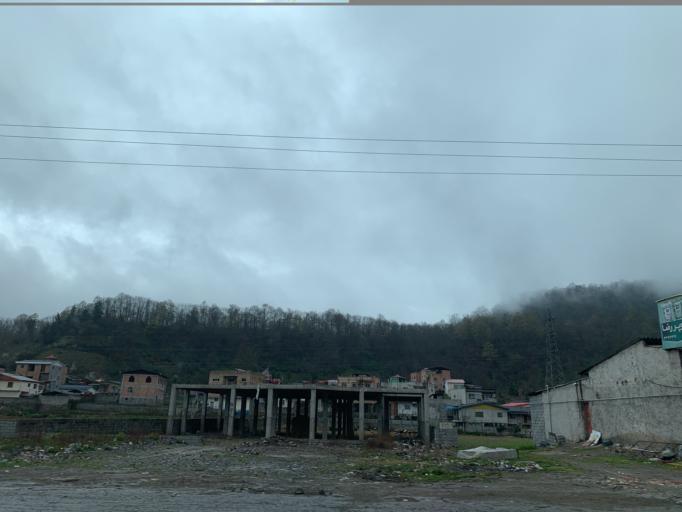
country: IR
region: Mazandaran
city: Amol
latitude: 36.3677
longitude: 52.3559
